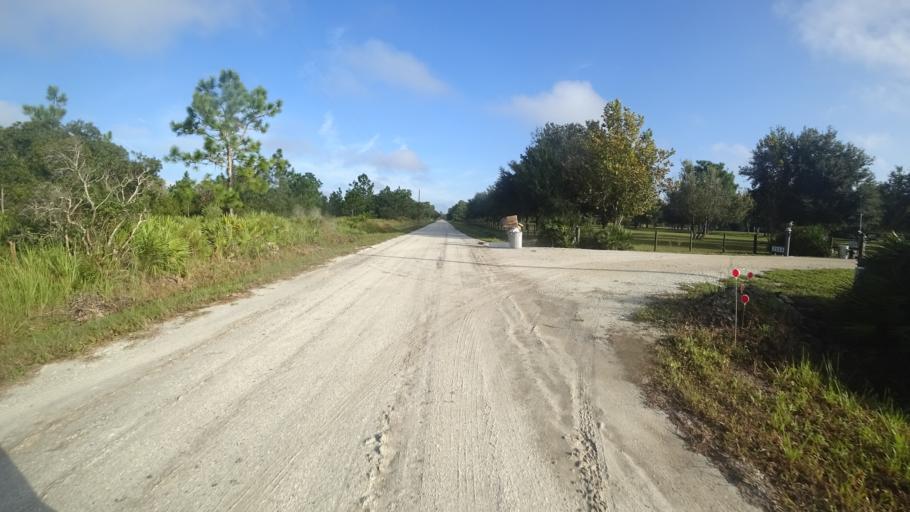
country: US
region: Florida
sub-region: Sarasota County
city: The Meadows
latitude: 27.4088
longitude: -82.2915
